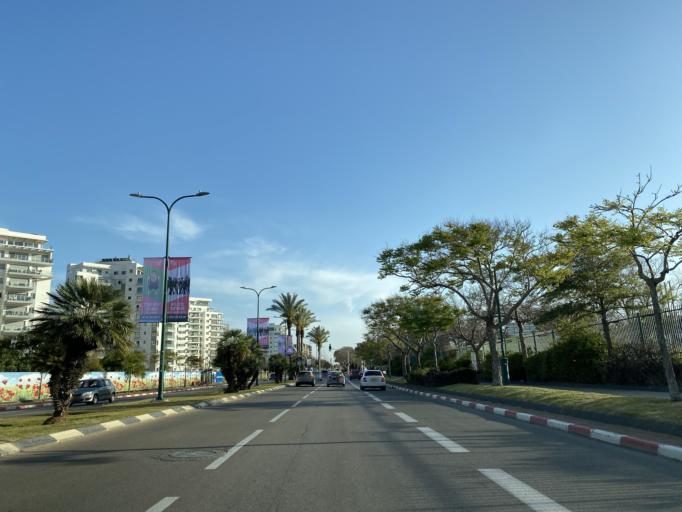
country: IL
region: Tel Aviv
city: Herzliyya
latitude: 32.1680
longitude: 34.8284
